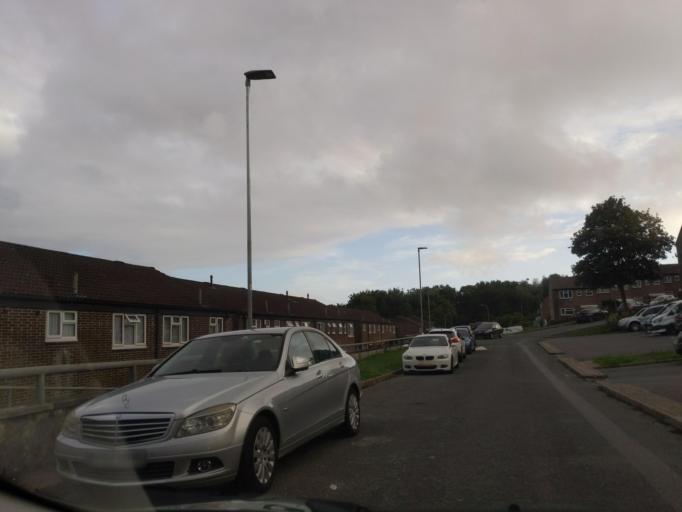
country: GB
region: England
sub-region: Devon
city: Plympton
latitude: 50.4049
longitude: -4.0909
